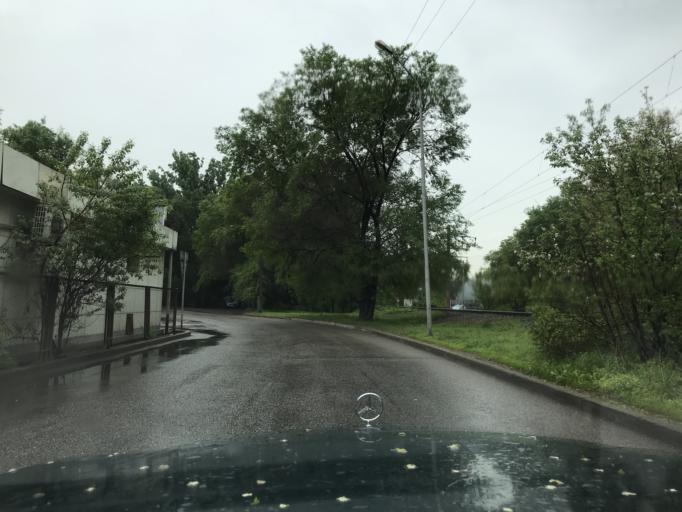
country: KZ
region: Almaty Oblysy
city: Pervomayskiy
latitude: 43.3307
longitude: 76.9593
